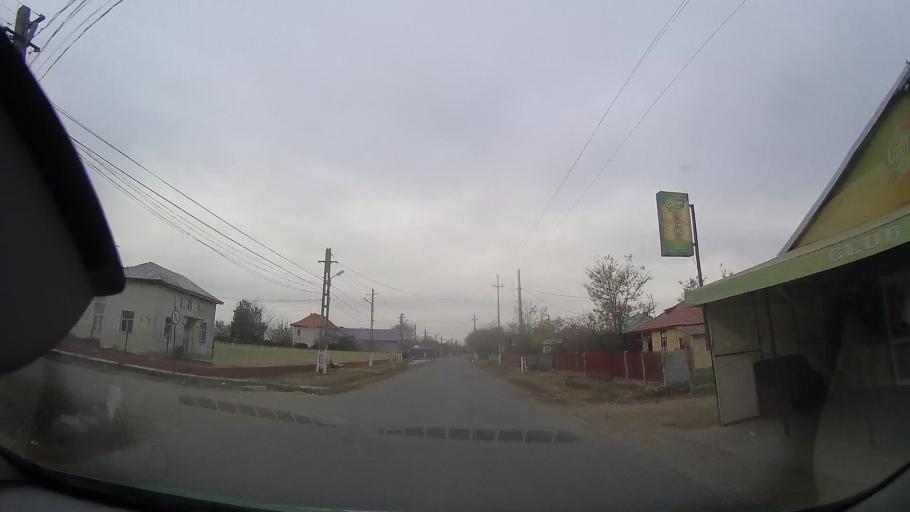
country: RO
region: Buzau
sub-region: Comuna Largu
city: Largu
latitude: 44.9750
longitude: 27.1473
